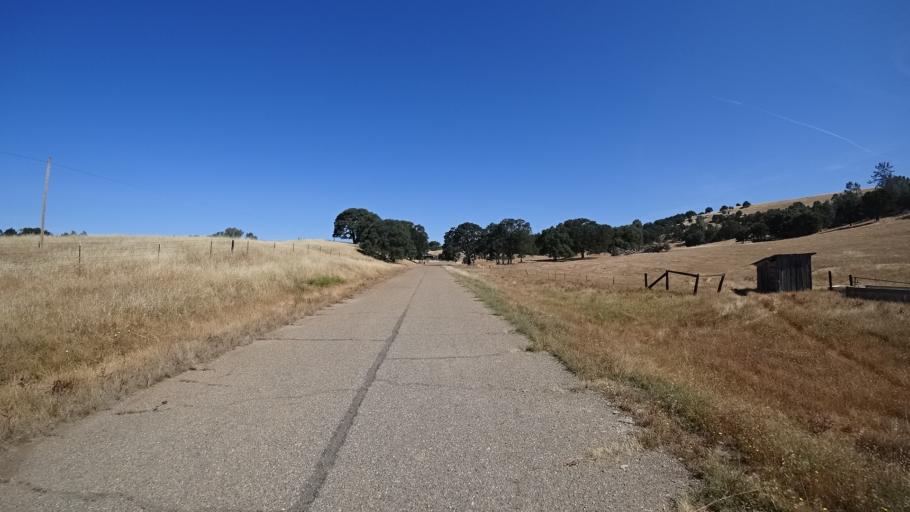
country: US
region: California
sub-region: Calaveras County
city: Valley Springs
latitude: 38.2303
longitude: -120.8555
